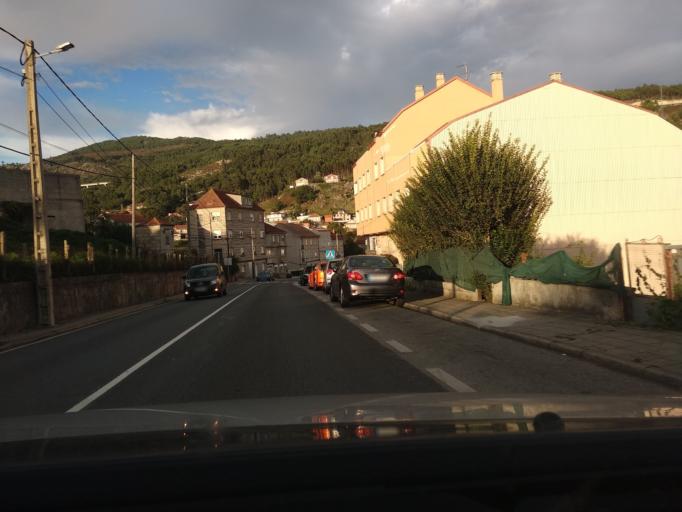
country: ES
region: Galicia
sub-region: Provincia de Pontevedra
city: Moana
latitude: 42.2888
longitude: -8.7201
